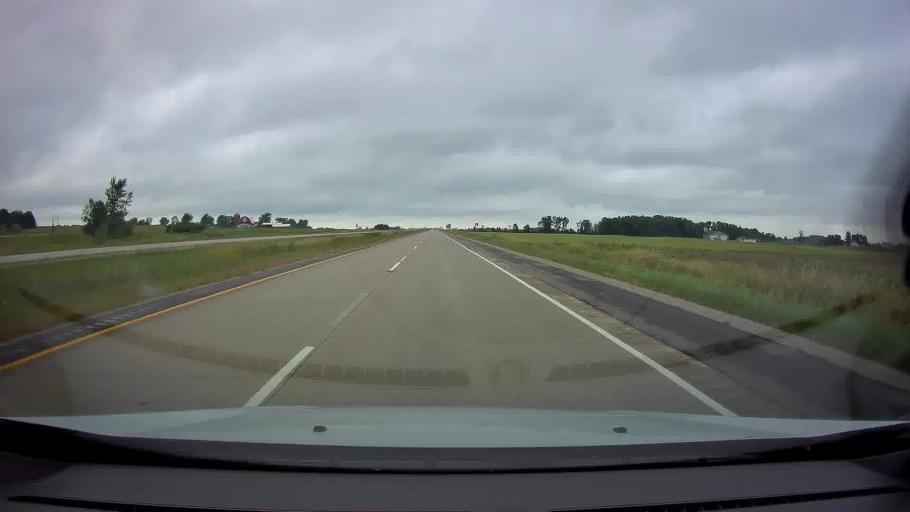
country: US
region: Wisconsin
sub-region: Brown County
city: Pulaski
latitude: 44.6638
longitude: -88.3047
